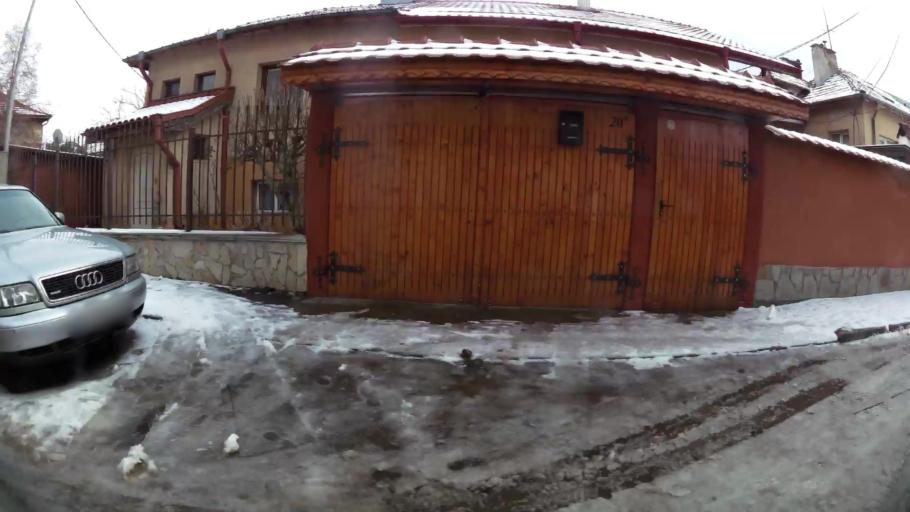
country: BG
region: Sofia-Capital
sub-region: Stolichna Obshtina
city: Sofia
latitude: 42.6985
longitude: 23.3799
